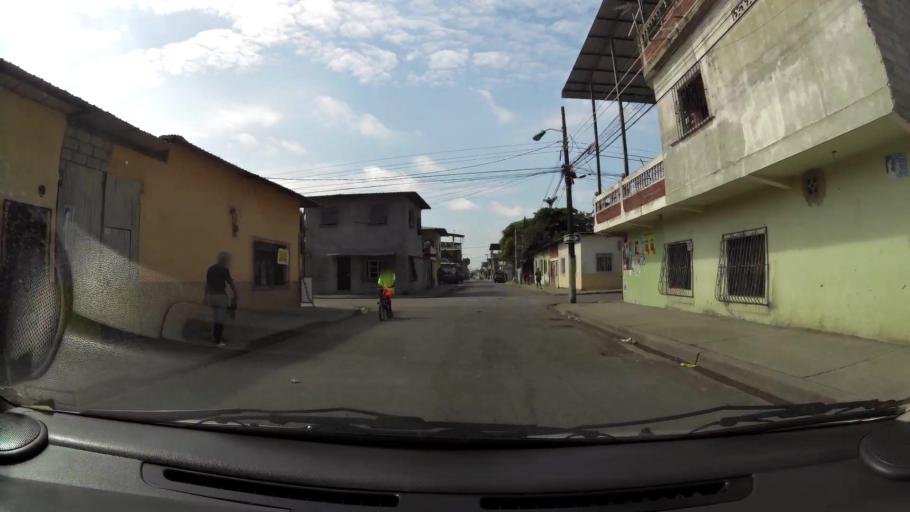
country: EC
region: Guayas
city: Guayaquil
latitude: -2.2729
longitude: -79.8946
